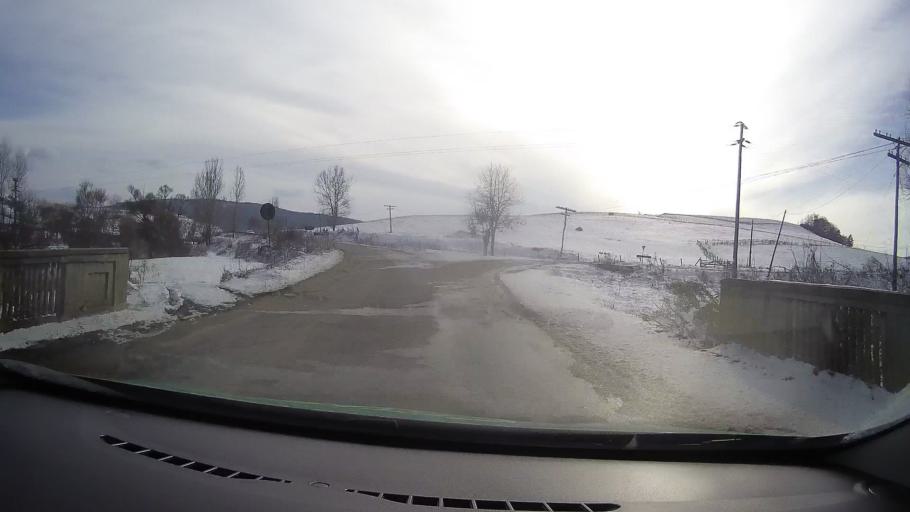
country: RO
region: Sibiu
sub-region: Oras Agnita
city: Ruja
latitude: 46.0018
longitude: 24.6727
